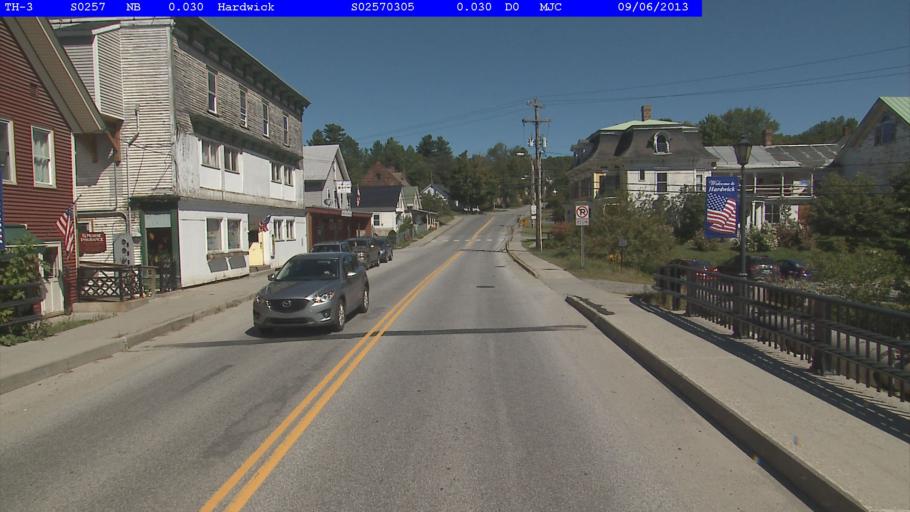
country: US
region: Vermont
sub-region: Caledonia County
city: Hardwick
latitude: 44.5049
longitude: -72.3659
